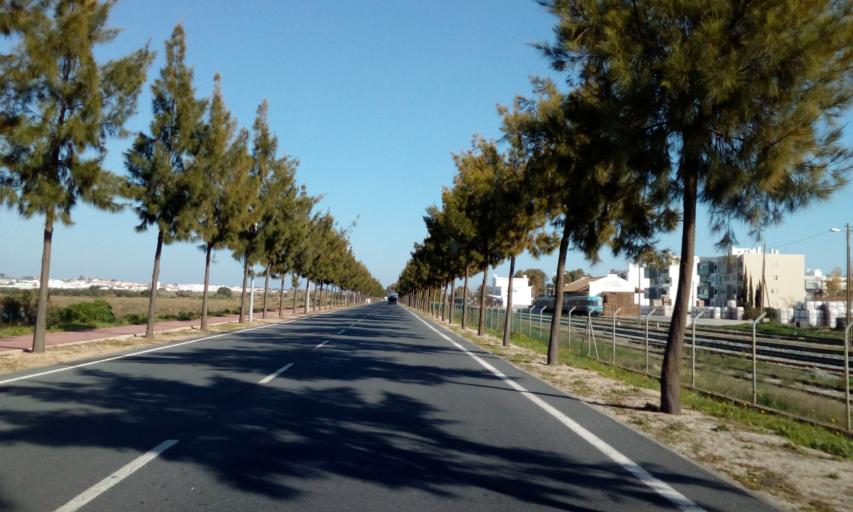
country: PT
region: Faro
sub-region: Vila Real de Santo Antonio
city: Vila Real de Santo Antonio
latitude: 37.1986
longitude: -7.4241
